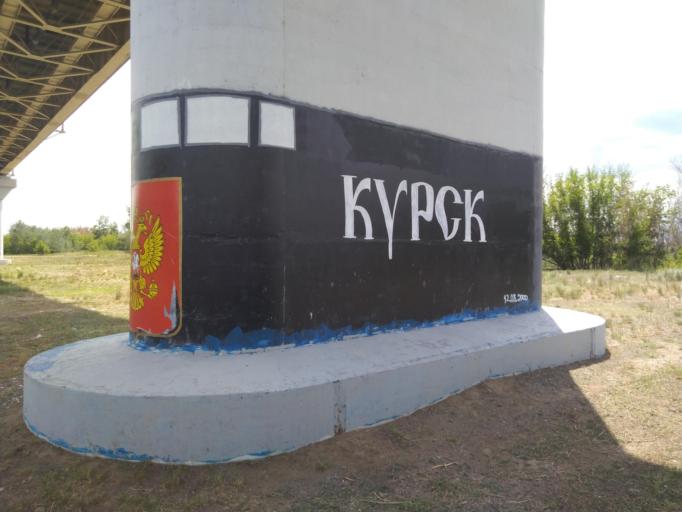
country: RU
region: Orenburg
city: Novotroitsk
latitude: 51.2018
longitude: 58.4363
